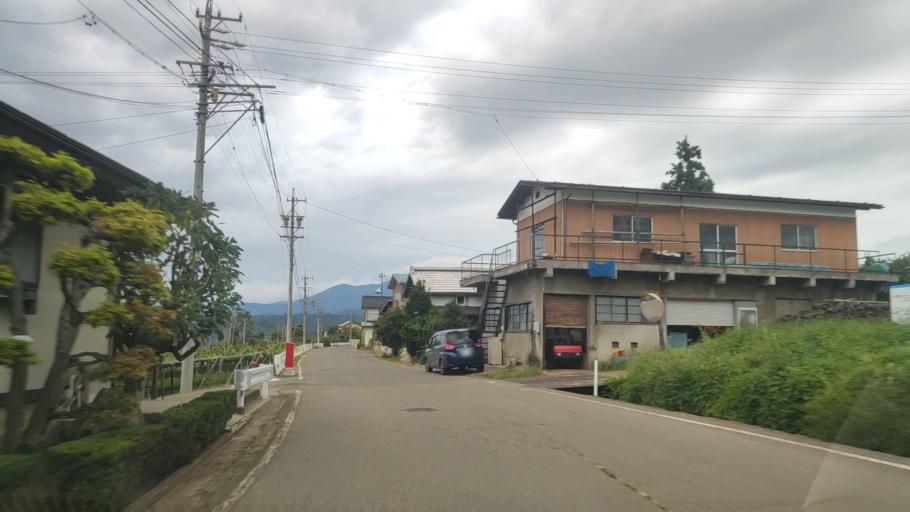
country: JP
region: Nagano
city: Nakano
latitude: 36.7807
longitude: 138.3733
